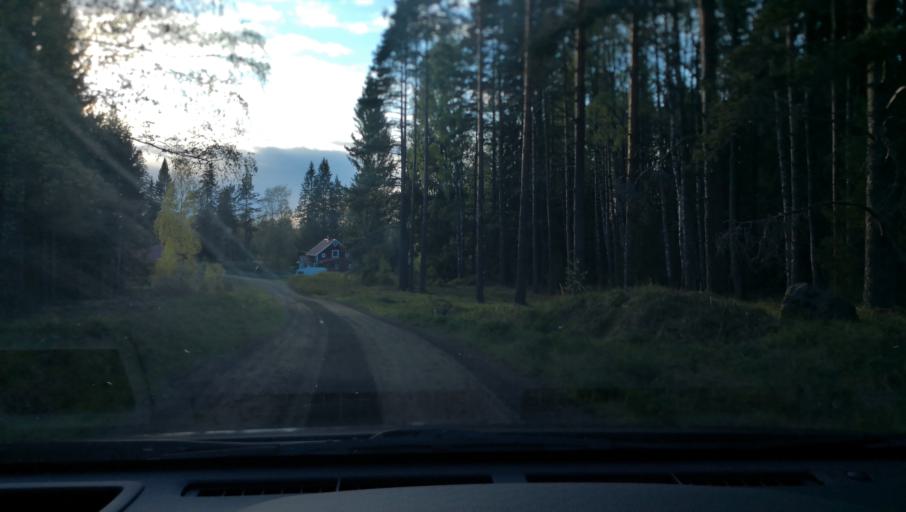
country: SE
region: OErebro
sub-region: Askersunds Kommun
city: Asbro
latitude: 58.8864
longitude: 15.1243
